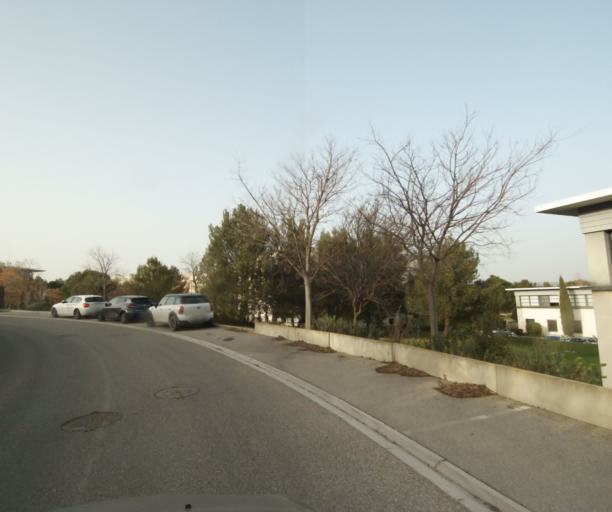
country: FR
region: Provence-Alpes-Cote d'Azur
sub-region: Departement des Bouches-du-Rhone
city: Cabries
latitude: 43.4943
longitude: 5.3490
